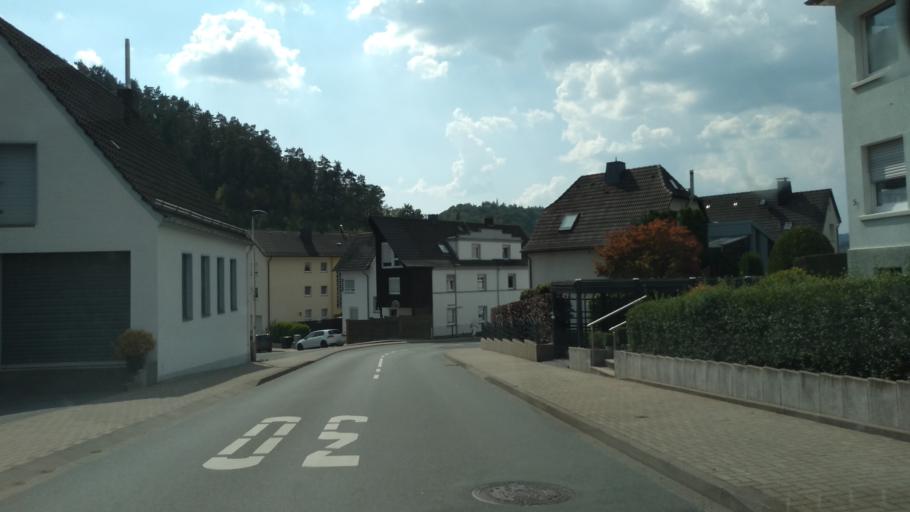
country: DE
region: North Rhine-Westphalia
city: Plettenberg
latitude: 51.2109
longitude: 7.8860
